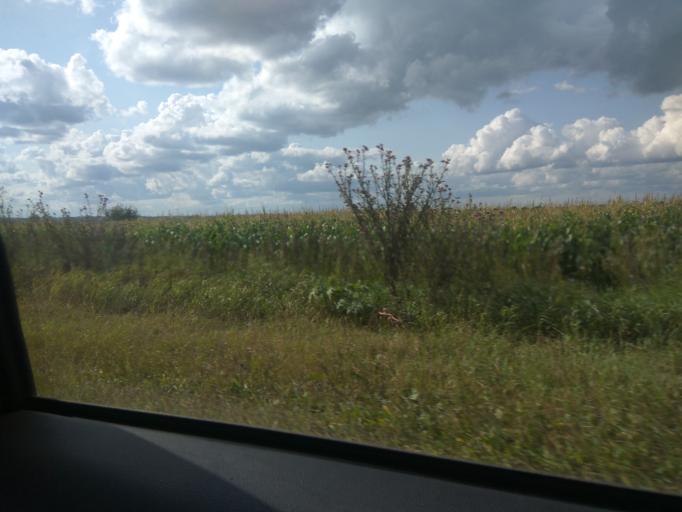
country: RU
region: Moskovskaya
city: Ramenskoye
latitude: 55.5095
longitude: 38.2568
